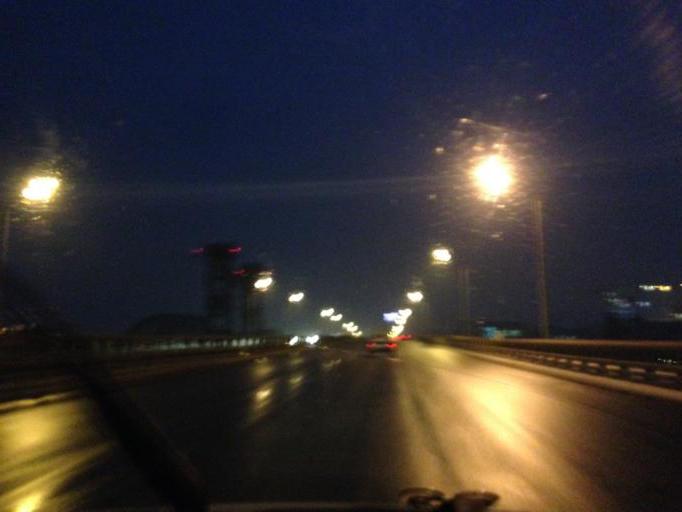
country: RU
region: Rostov
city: Rostov-na-Donu
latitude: 47.2077
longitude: 39.7047
